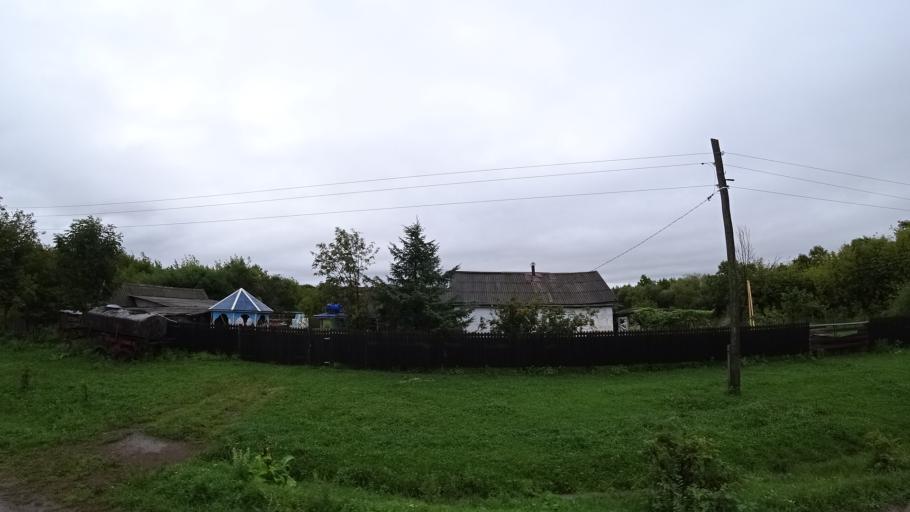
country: RU
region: Primorskiy
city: Monastyrishche
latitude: 44.2609
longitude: 132.4245
